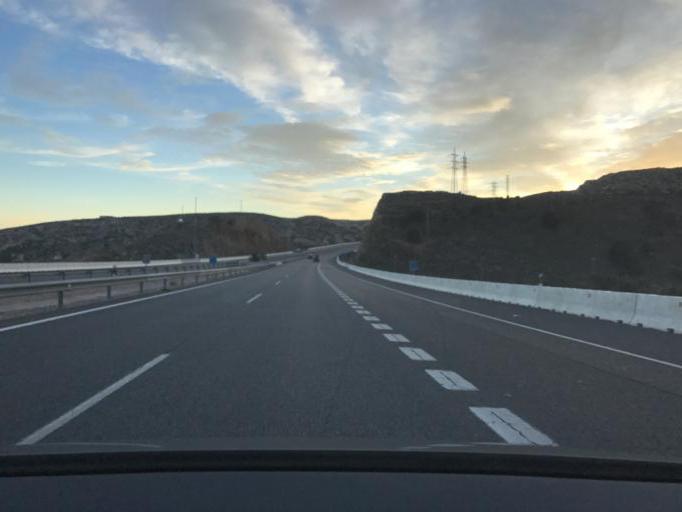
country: ES
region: Andalusia
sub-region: Provincia de Almeria
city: Almeria
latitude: 36.8548
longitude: -2.4733
